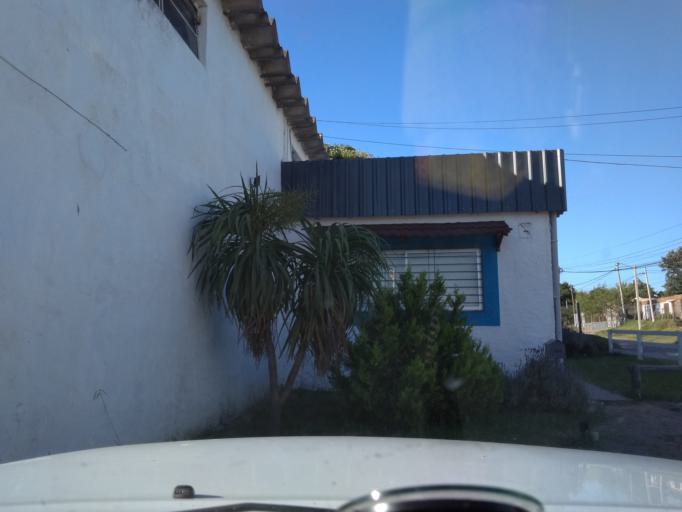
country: UY
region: Florida
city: Florida
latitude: -34.0838
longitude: -56.2130
